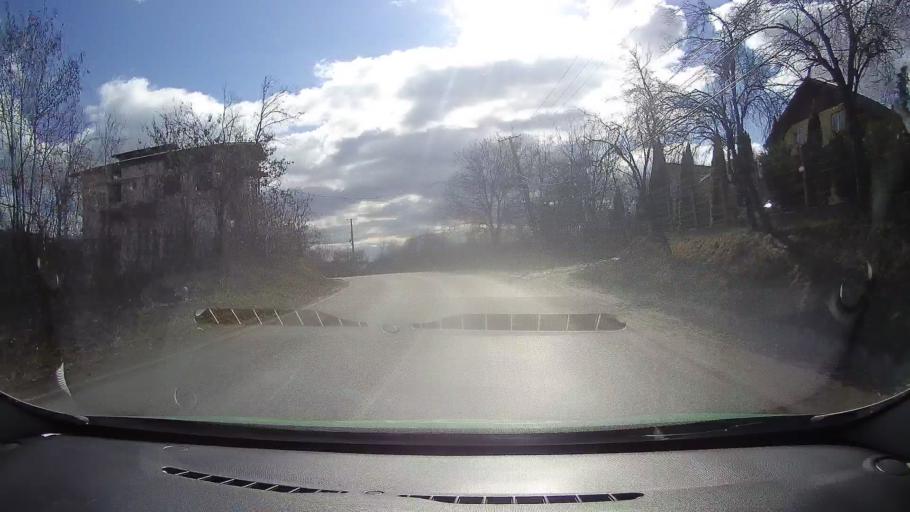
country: RO
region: Dambovita
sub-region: Comuna Motaeni
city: Motaeni
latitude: 45.1089
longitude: 25.4141
